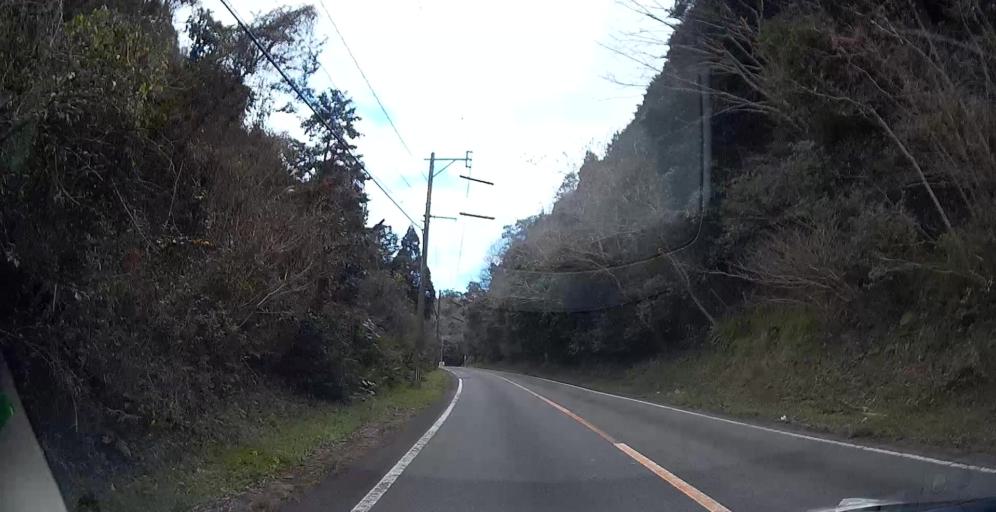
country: JP
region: Kumamoto
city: Yatsushiro
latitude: 32.3709
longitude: 130.5047
